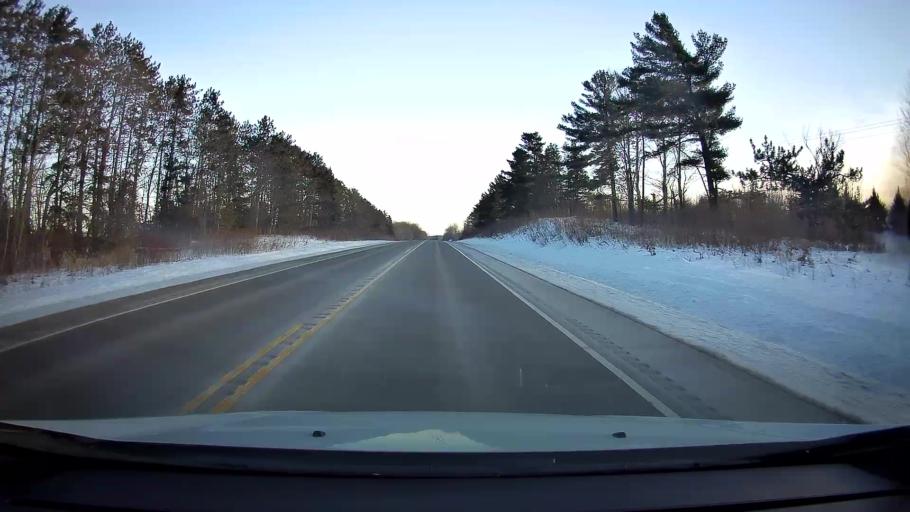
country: US
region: Wisconsin
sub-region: Washburn County
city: Shell Lake
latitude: 45.6938
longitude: -91.9663
